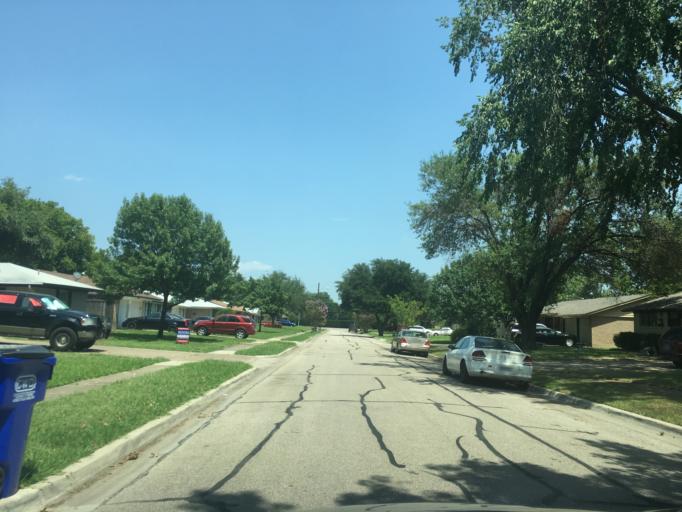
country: US
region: Texas
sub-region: Dallas County
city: Carrollton
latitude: 32.9364
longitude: -96.8755
